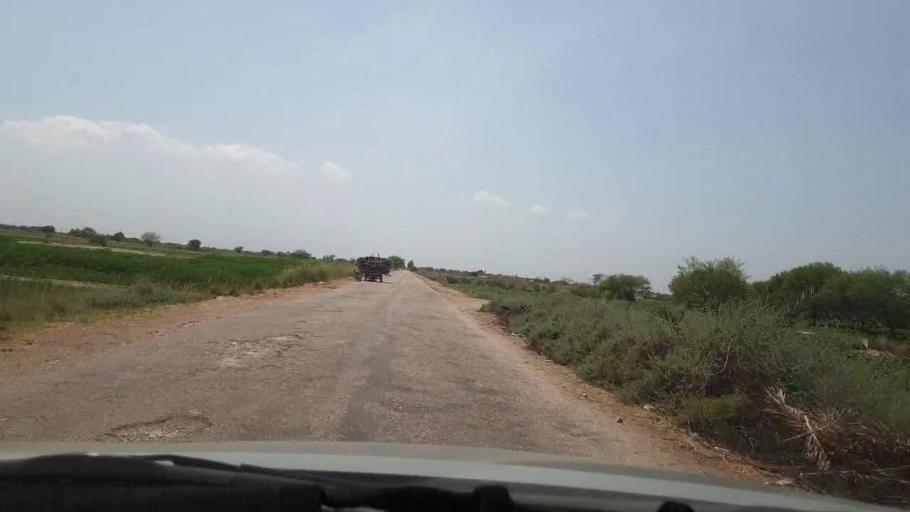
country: PK
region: Sindh
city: Rohri
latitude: 27.6695
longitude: 69.0733
